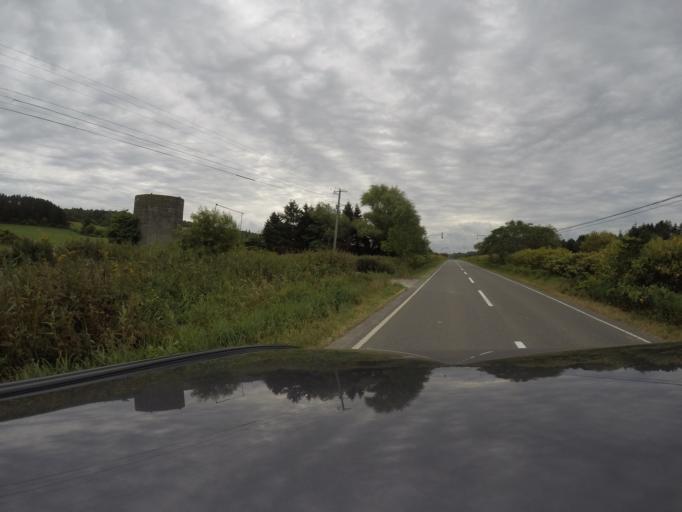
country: JP
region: Hokkaido
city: Makubetsu
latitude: 45.1899
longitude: 141.7404
